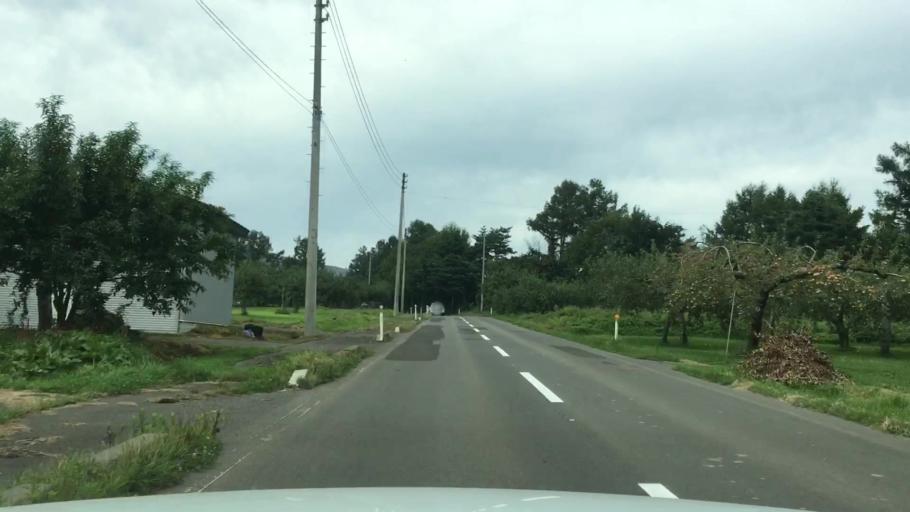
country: JP
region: Aomori
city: Hirosaki
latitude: 40.6772
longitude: 140.3786
